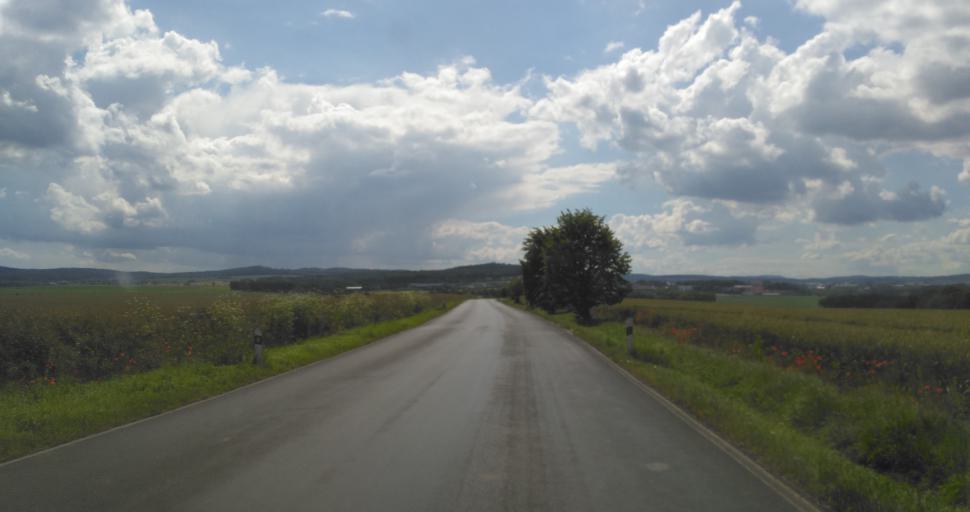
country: CZ
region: Central Bohemia
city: Lochovice
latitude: 49.8433
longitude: 13.9473
